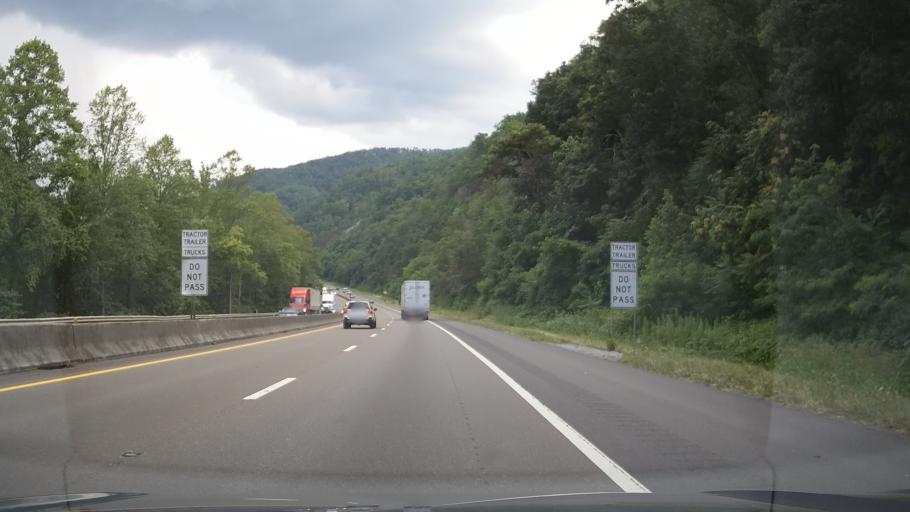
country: US
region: Tennessee
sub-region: Cocke County
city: Newport
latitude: 35.8307
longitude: -83.1830
